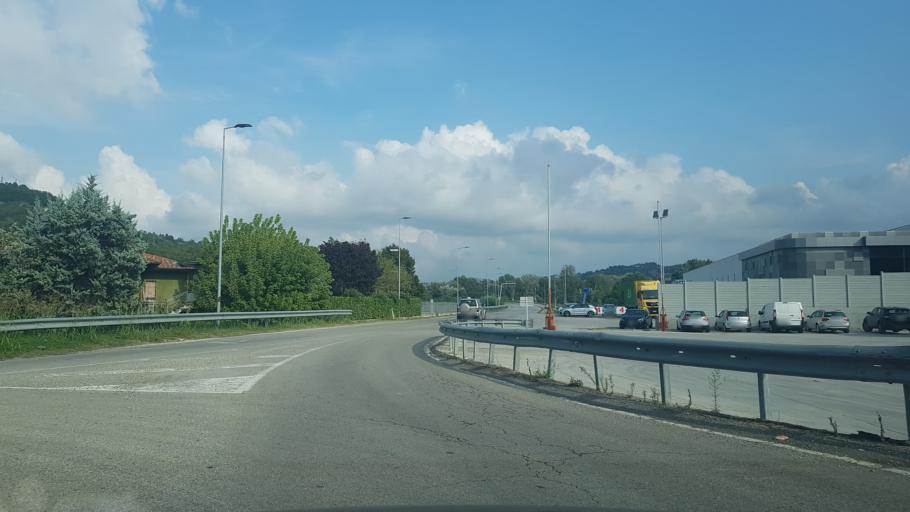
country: IT
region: Piedmont
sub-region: Provincia di Cuneo
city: Santo Stefano Belbo
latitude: 44.7119
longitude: 8.2434
